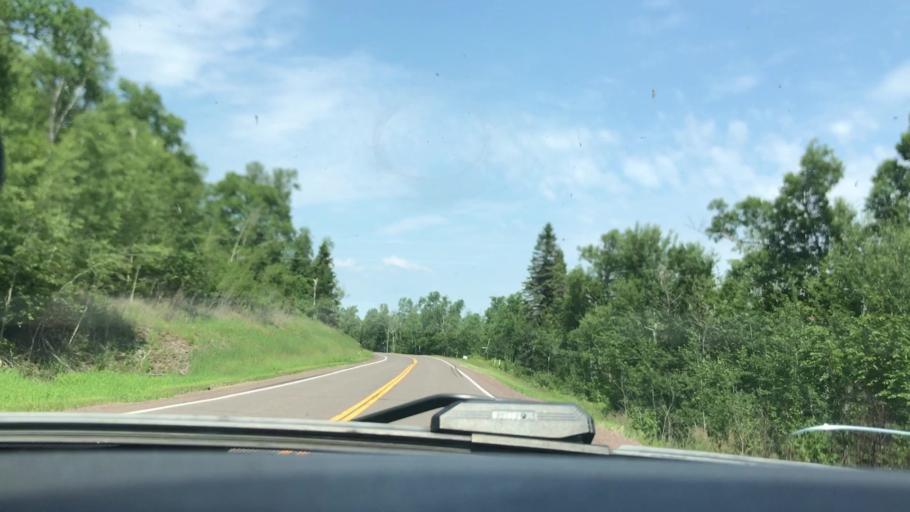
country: US
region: Minnesota
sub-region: Lake County
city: Silver Bay
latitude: 47.4951
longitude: -90.9730
